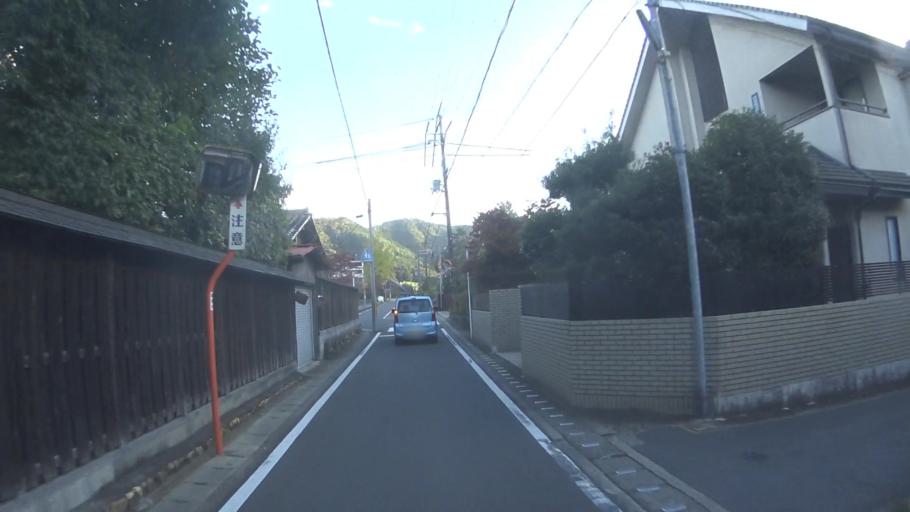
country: JP
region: Kyoto
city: Ayabe
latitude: 35.2943
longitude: 135.2575
